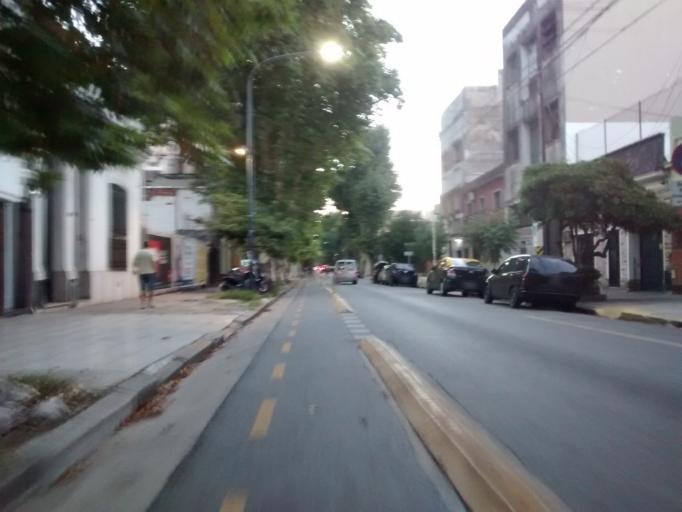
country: AR
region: Buenos Aires F.D.
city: Villa Santa Rita
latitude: -34.6068
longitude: -58.4560
